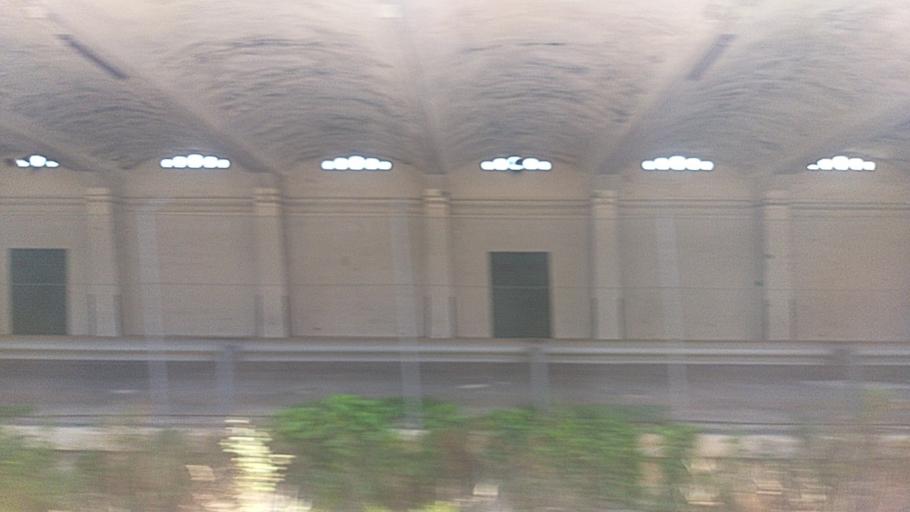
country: PT
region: Lisbon
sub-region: Lisbon
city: Lisbon
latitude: 38.7325
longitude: -9.1086
